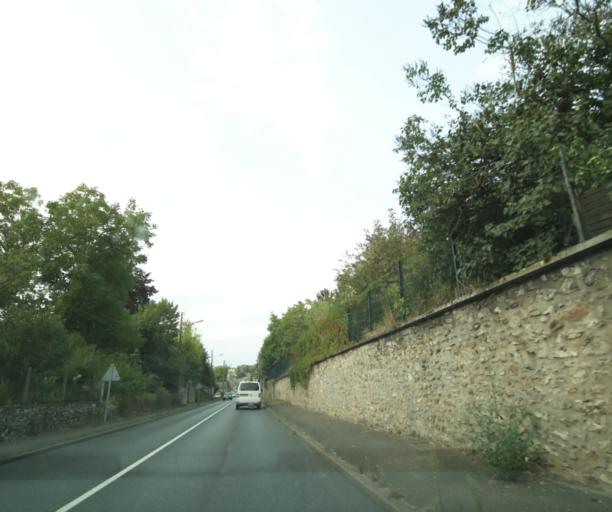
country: FR
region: Centre
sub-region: Departement d'Indre-et-Loire
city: Cormery
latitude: 47.2643
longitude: 0.8359
